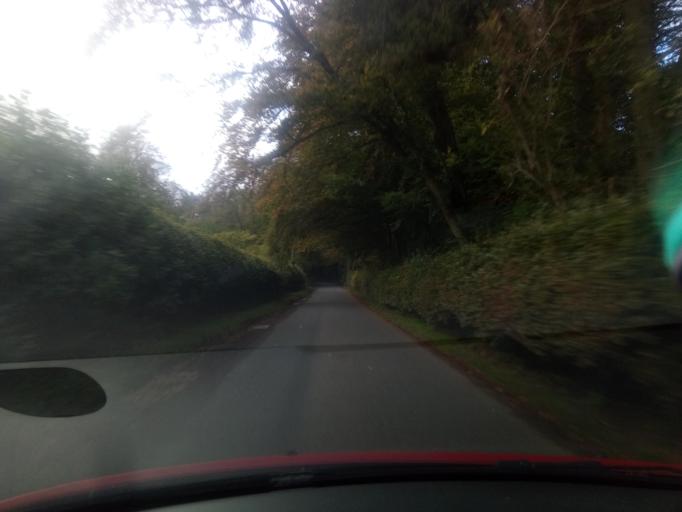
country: GB
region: Scotland
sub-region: The Scottish Borders
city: Jedburgh
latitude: 55.3788
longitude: -2.6468
